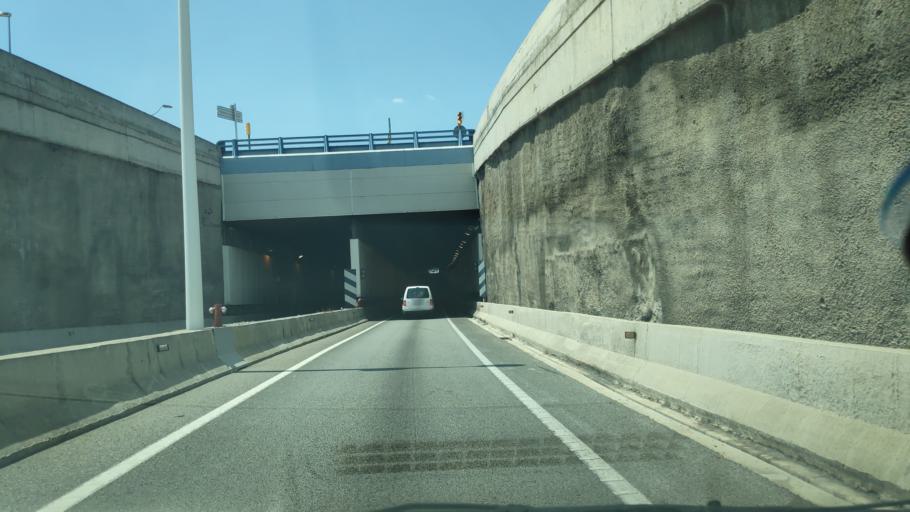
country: ES
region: Catalonia
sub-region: Provincia de Barcelona
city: Les Franqueses del Valles
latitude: 41.6226
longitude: 2.2948
